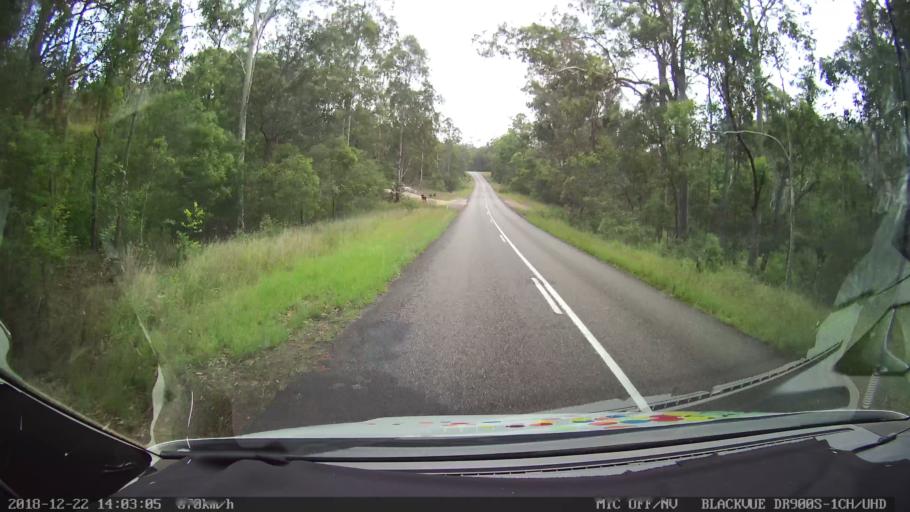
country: AU
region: New South Wales
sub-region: Clarence Valley
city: Coutts Crossing
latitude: -29.9273
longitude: 152.7422
